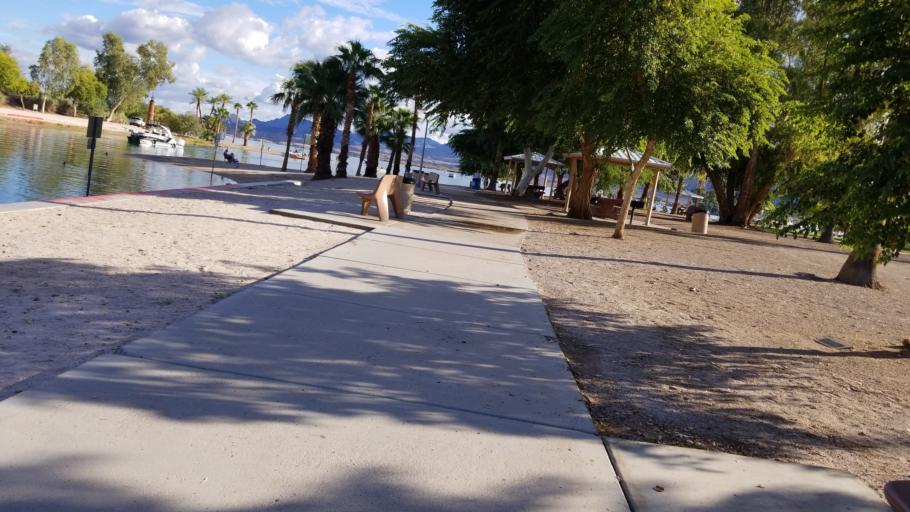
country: US
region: Arizona
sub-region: Mohave County
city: Lake Havasu City
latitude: 34.4665
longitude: -114.3475
